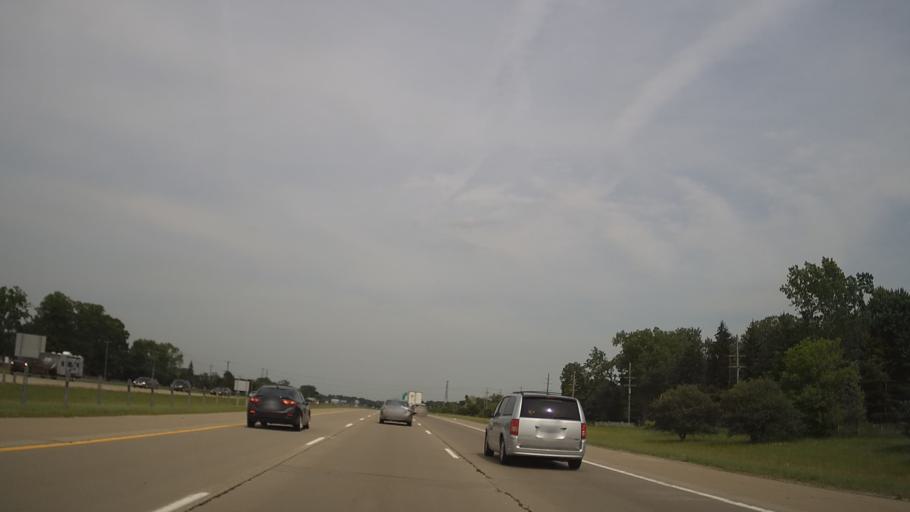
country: US
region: Michigan
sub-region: Wayne County
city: Belleville
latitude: 42.2198
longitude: -83.4692
